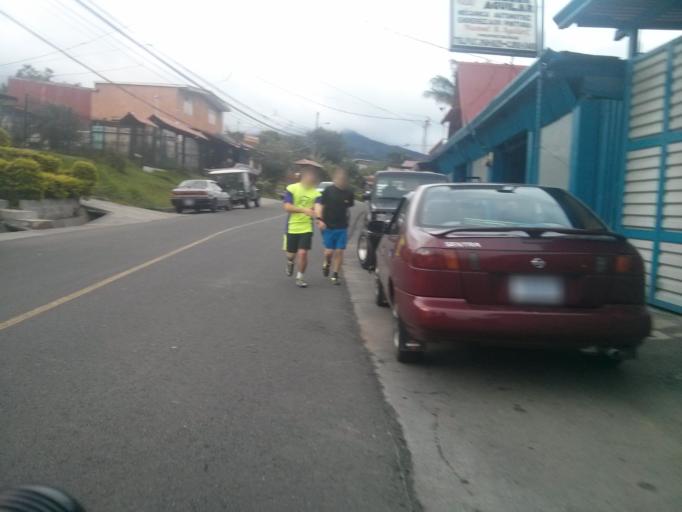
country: CR
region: Heredia
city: Angeles
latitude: 10.0202
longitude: -84.0517
